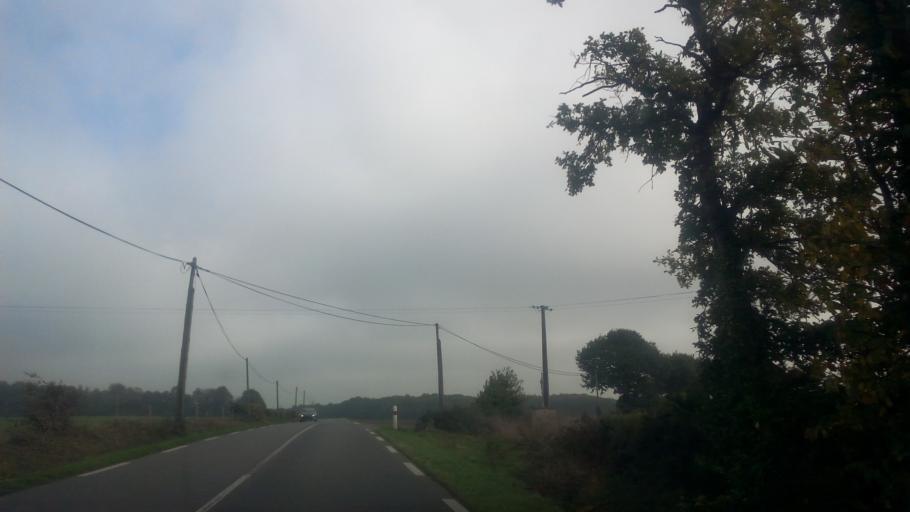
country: FR
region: Pays de la Loire
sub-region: Departement de la Loire-Atlantique
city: Avessac
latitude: 47.6354
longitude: -1.9488
